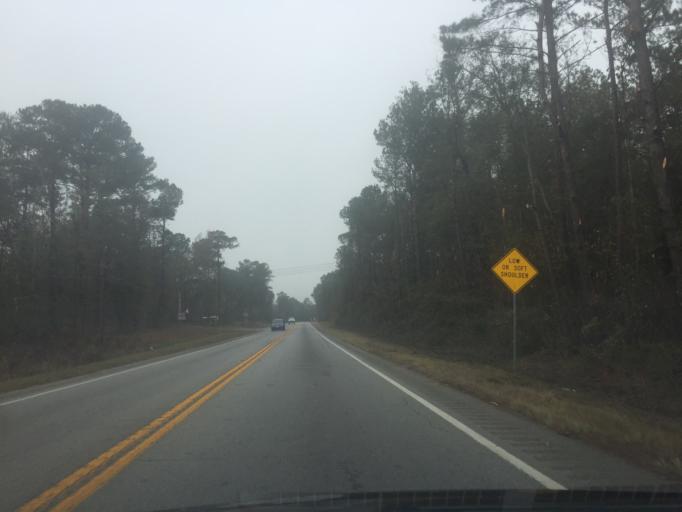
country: US
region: Georgia
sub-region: Chatham County
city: Georgetown
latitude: 32.0076
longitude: -81.2893
